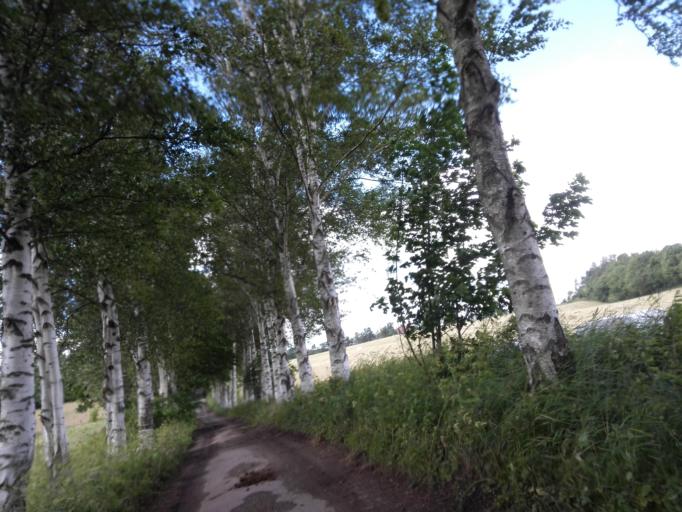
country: DK
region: Capital Region
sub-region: Allerod Kommune
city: Lynge
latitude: 55.8204
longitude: 12.2891
